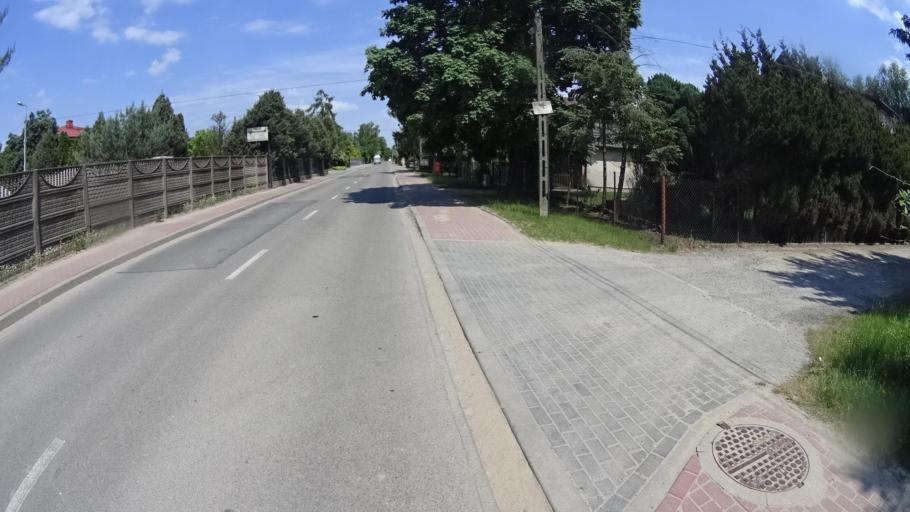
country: PL
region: Masovian Voivodeship
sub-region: Powiat warszawski zachodni
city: Stare Babice
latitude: 52.2556
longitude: 20.8308
